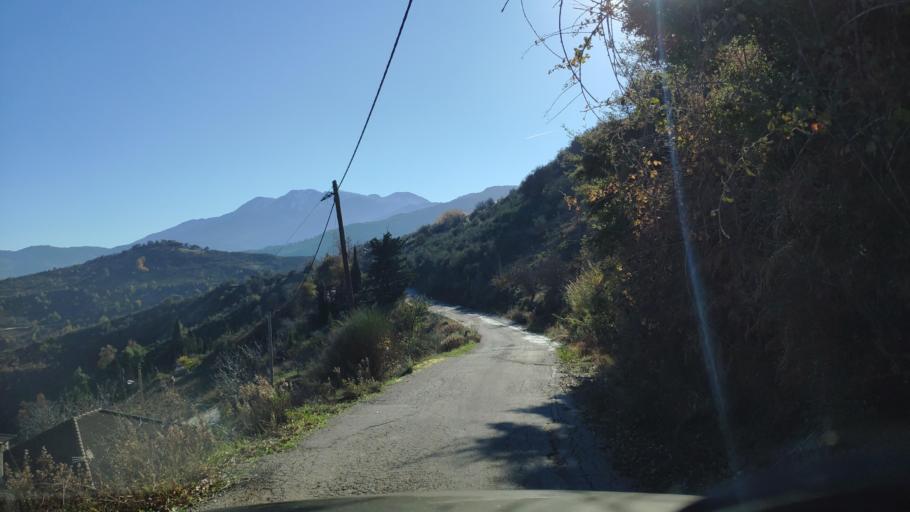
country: GR
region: Peloponnese
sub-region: Nomos Korinthias
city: Xylokastro
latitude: 38.0340
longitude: 22.4748
